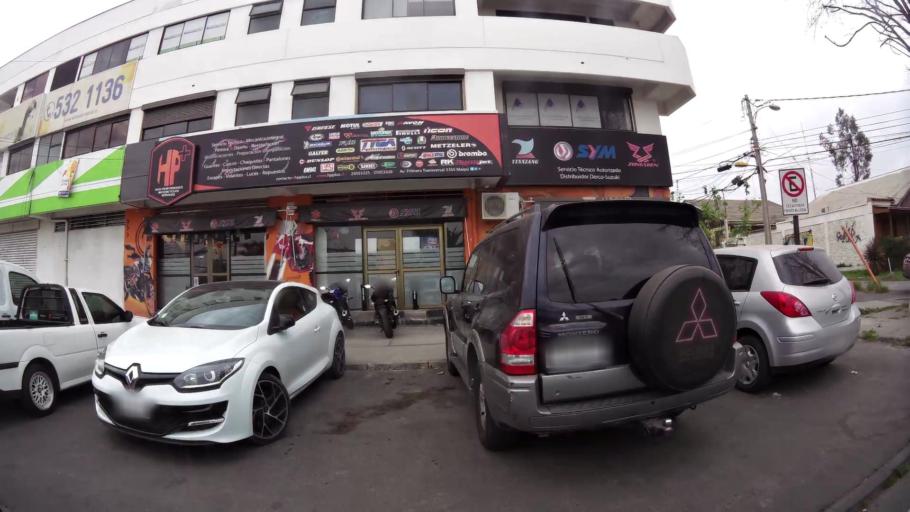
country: CL
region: Santiago Metropolitan
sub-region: Provincia de Santiago
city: Lo Prado
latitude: -33.4967
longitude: -70.7515
